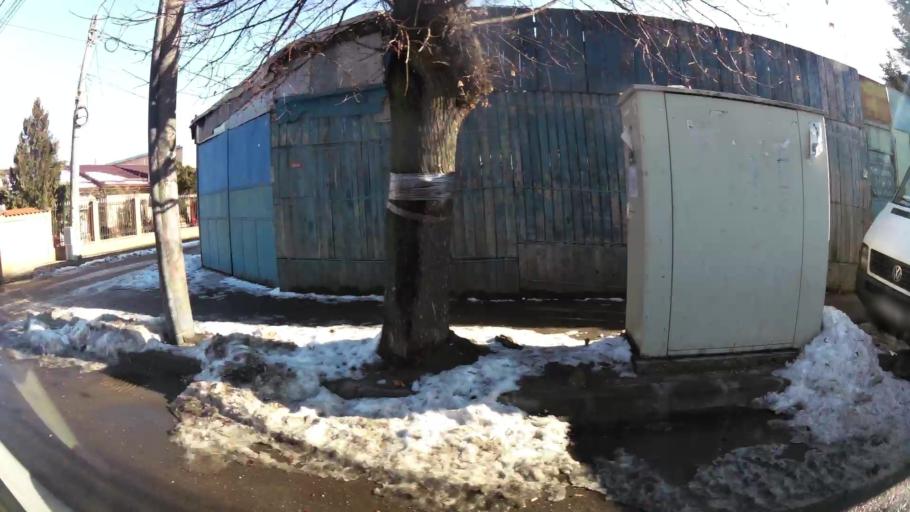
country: RO
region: Ilfov
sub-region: Comuna Magurele
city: Magurele
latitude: 44.3963
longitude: 26.0552
